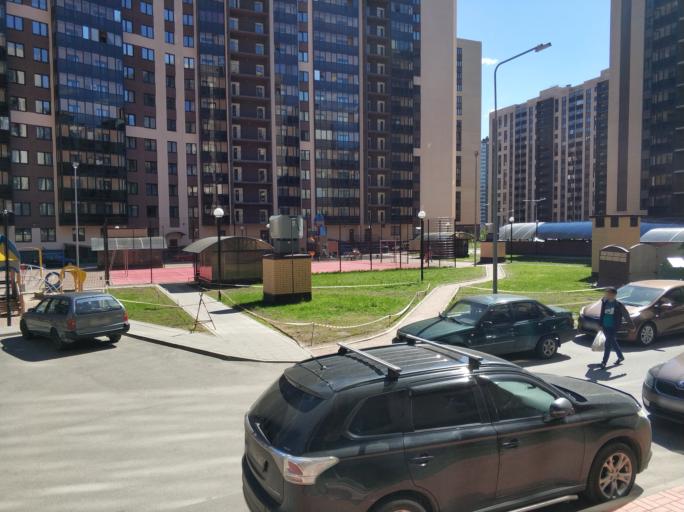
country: RU
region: Leningrad
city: Murino
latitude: 60.0540
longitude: 30.4300
